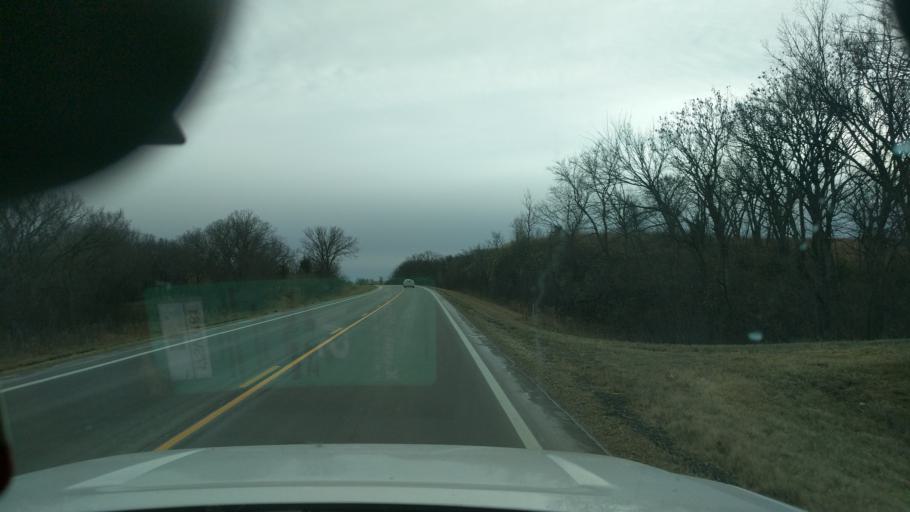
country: US
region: Kansas
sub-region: Geary County
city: Junction City
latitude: 38.9679
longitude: -96.8574
